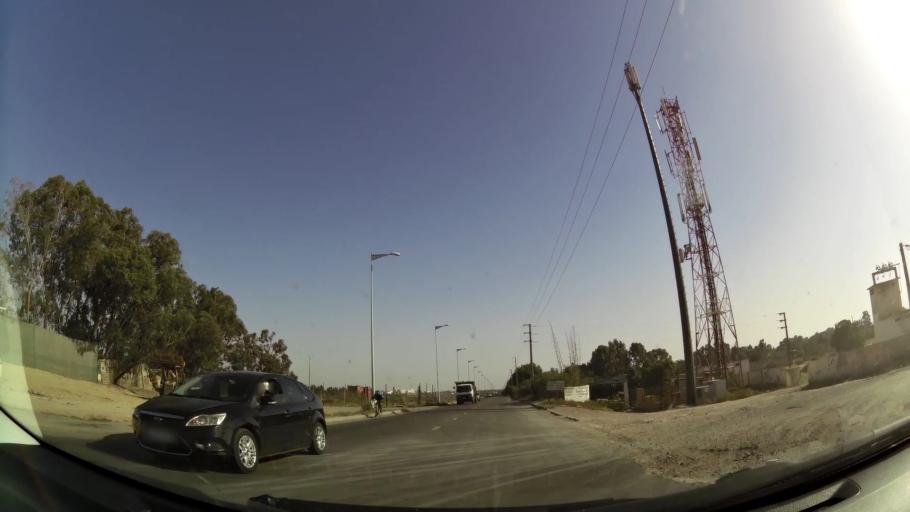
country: MA
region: Souss-Massa-Draa
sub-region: Inezgane-Ait Mellou
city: Inezgane
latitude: 30.3611
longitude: -9.5060
